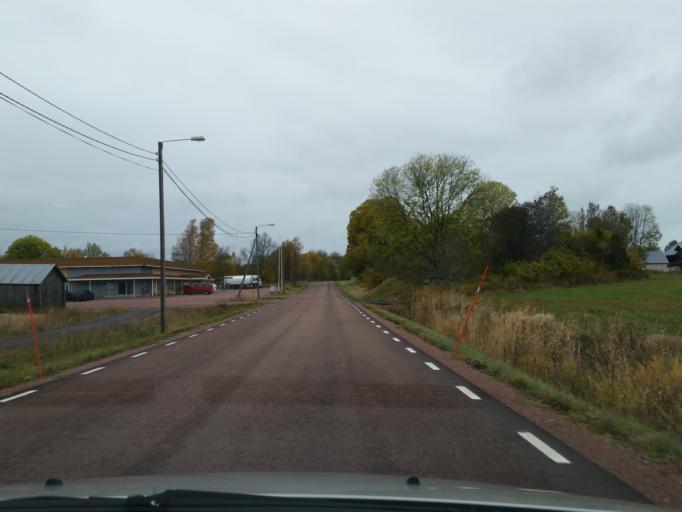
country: AX
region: Alands landsbygd
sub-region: Lemland
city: Lemland
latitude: 60.0696
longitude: 20.0860
